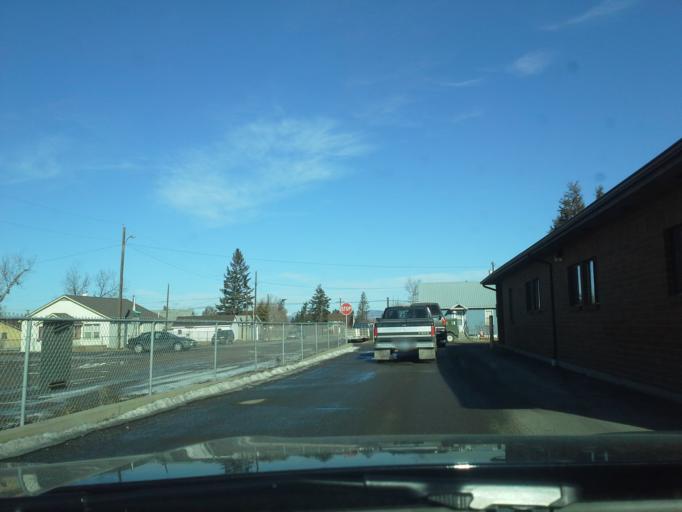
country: US
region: Montana
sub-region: Lewis and Clark County
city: East Helena
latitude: 46.5873
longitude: -111.9108
